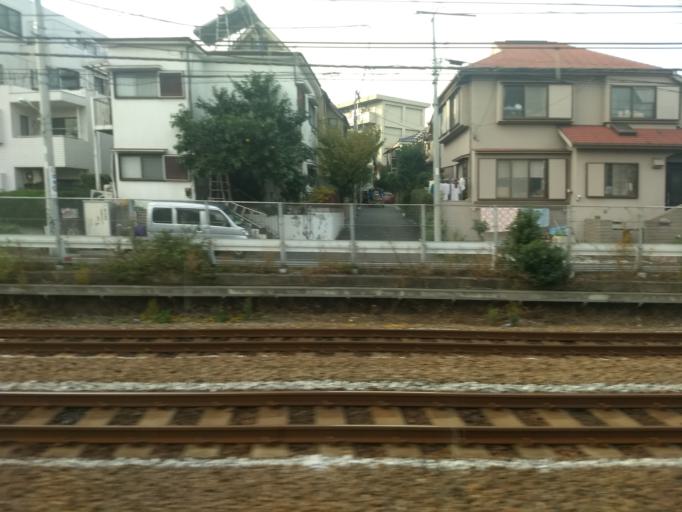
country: JP
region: Kanagawa
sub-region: Kawasaki-shi
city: Kawasaki
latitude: 35.5945
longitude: 139.7317
